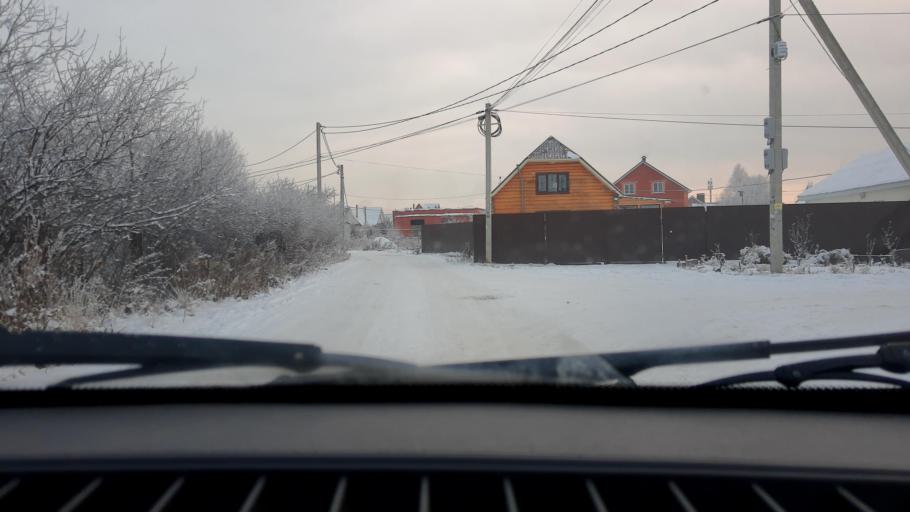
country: RU
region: Bashkortostan
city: Ufa
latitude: 54.6546
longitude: 55.9261
